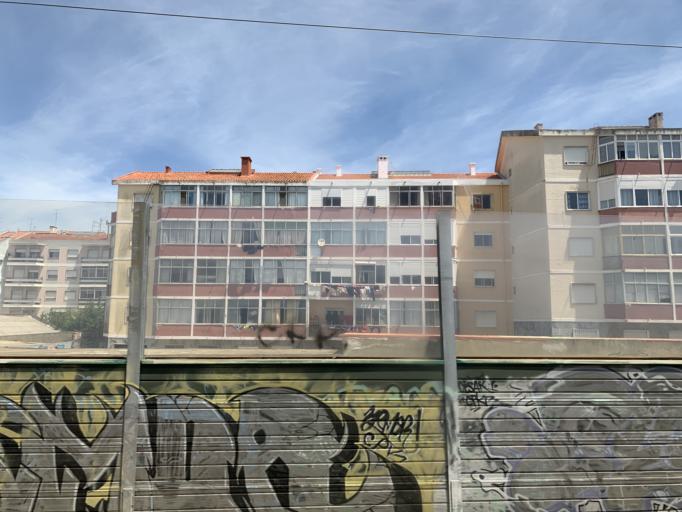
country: PT
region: Lisbon
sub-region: Sintra
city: Rio de Mouro
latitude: 38.7853
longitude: -9.3236
